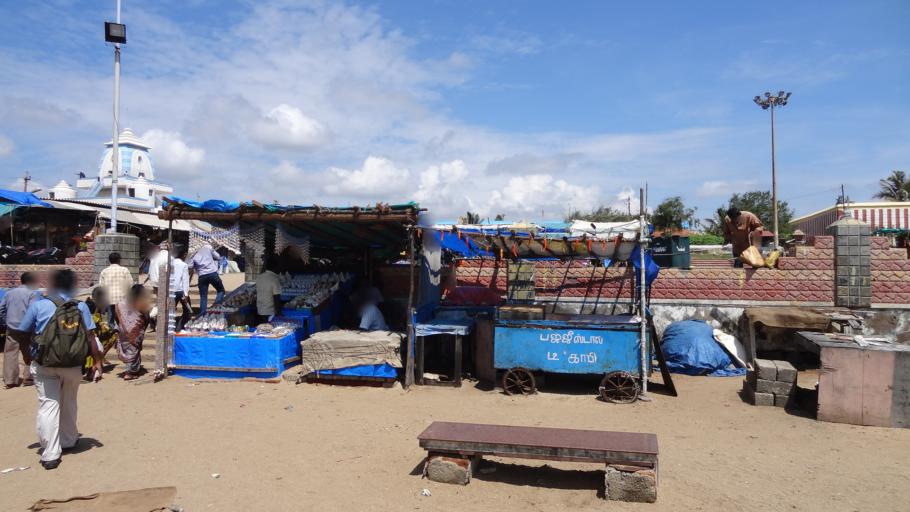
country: IN
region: Tamil Nadu
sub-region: Kanniyakumari
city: Kanniyakumari
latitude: 8.0783
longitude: 77.5506
